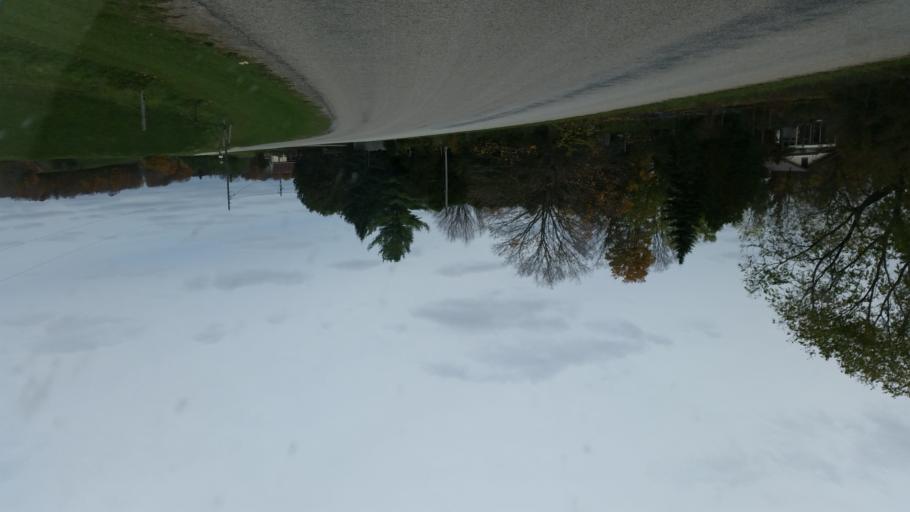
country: CA
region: Ontario
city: Wingham
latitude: 43.9776
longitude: -81.3325
